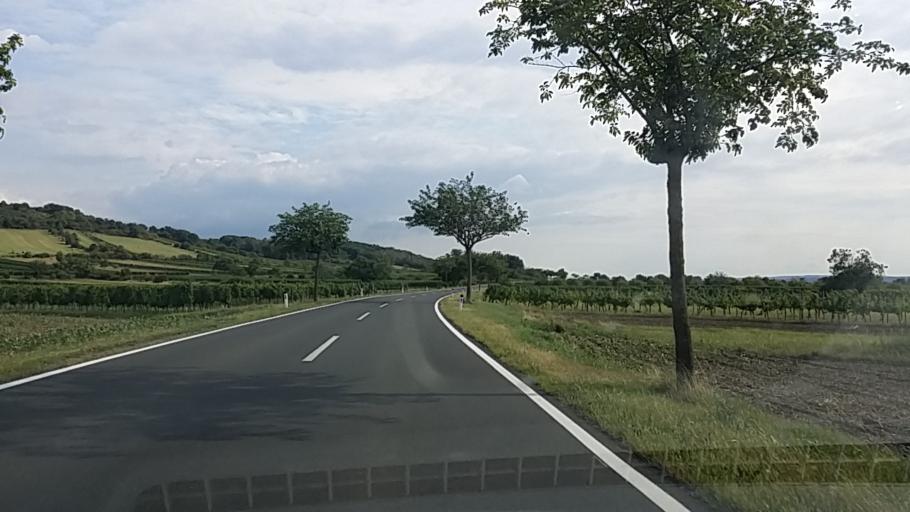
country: AT
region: Burgenland
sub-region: Eisenstadt-Umgebung
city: Schutzen am Gebirge
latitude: 47.8479
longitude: 16.6342
